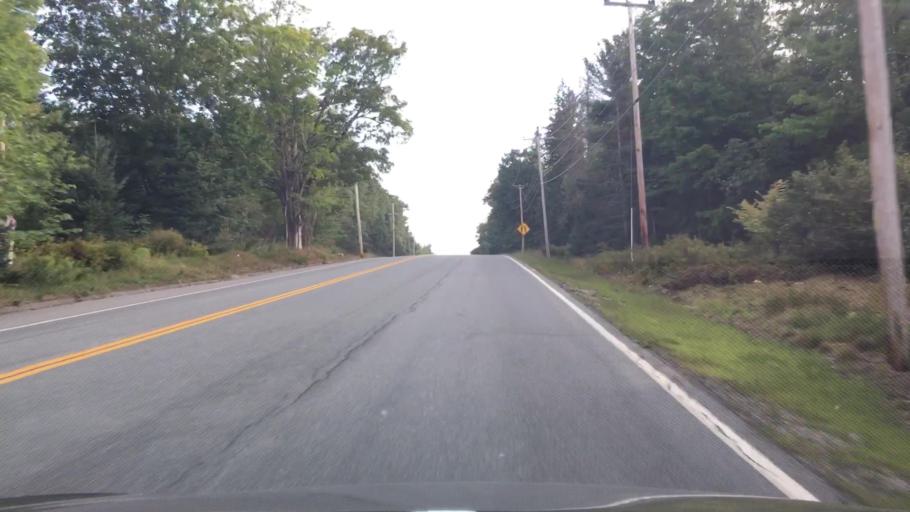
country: US
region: Maine
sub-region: Hancock County
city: Surry
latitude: 44.4902
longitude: -68.5097
